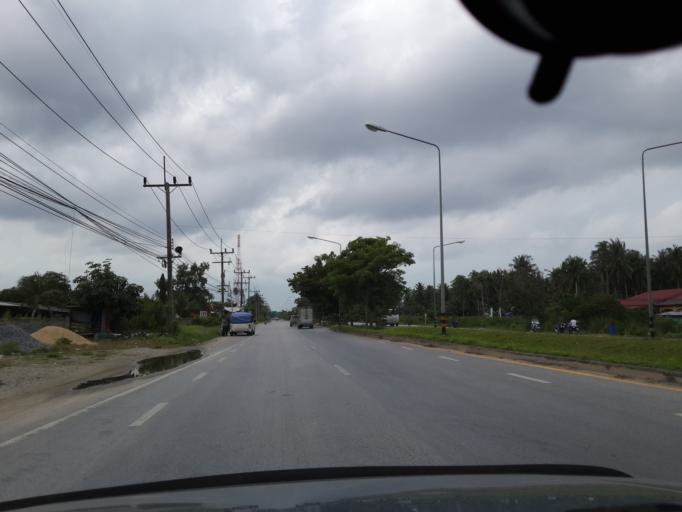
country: TH
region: Pattani
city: Pattani
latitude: 6.8718
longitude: 101.2906
